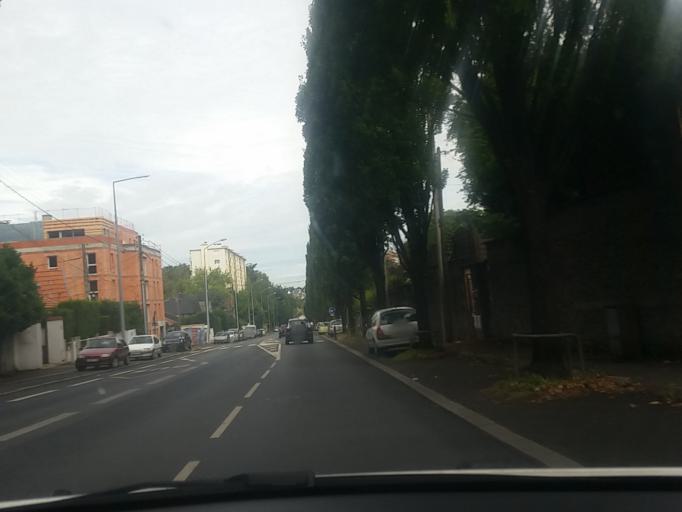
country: FR
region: Pays de la Loire
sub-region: Departement de la Loire-Atlantique
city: Nantes
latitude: 47.2426
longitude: -1.5741
